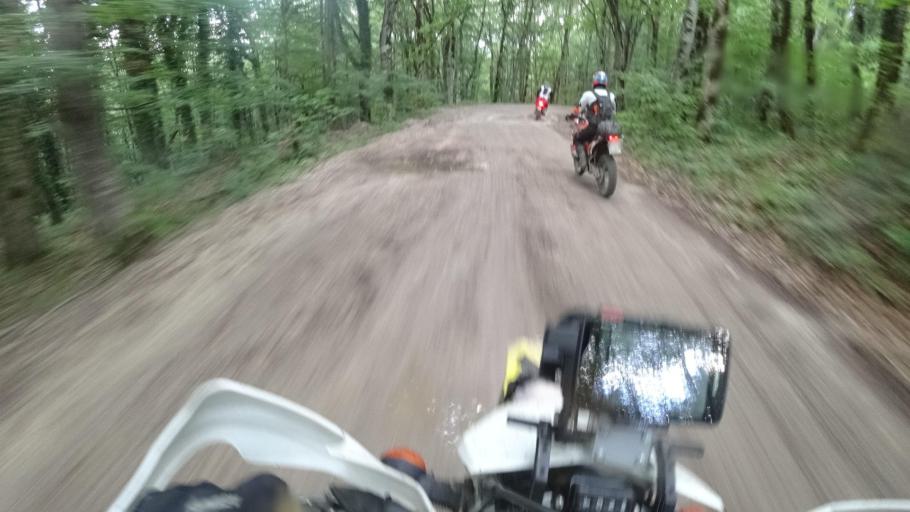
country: BA
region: Federation of Bosnia and Herzegovina
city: Sanica
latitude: 44.6710
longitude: 16.5564
